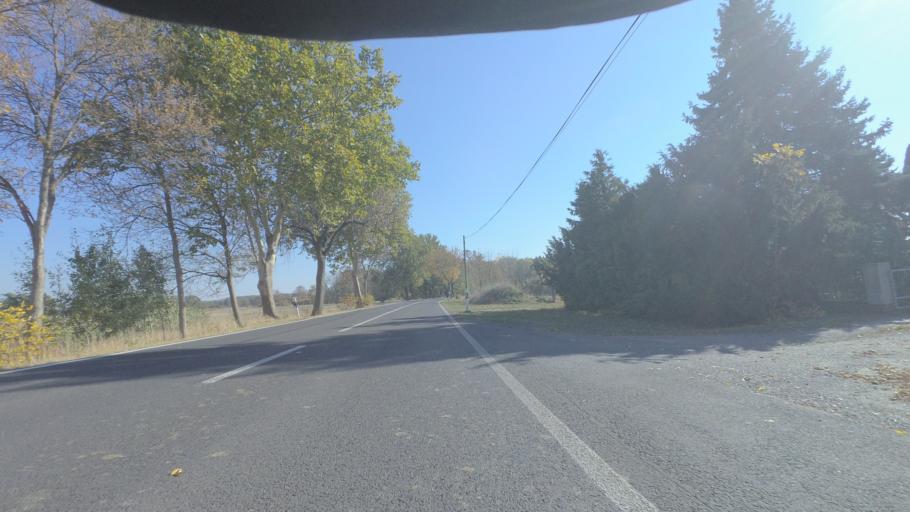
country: DE
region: Brandenburg
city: Zossen
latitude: 52.2558
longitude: 13.4601
